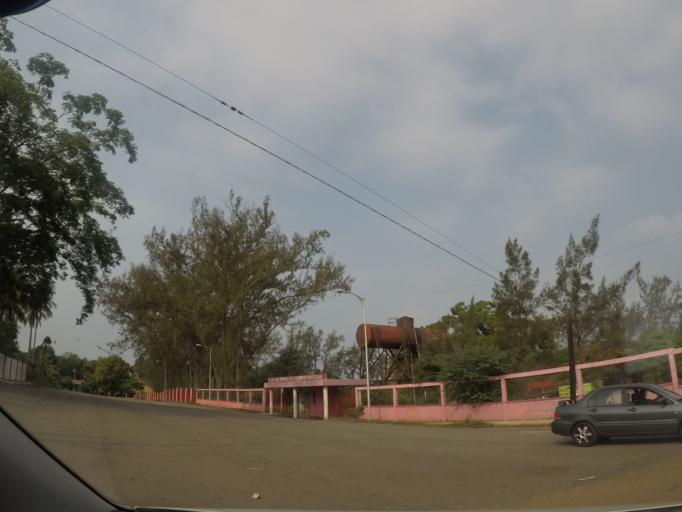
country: MX
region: Oaxaca
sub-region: Santa Maria Petapa
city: Llano Suchiapa
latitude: 16.8735
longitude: -95.0488
